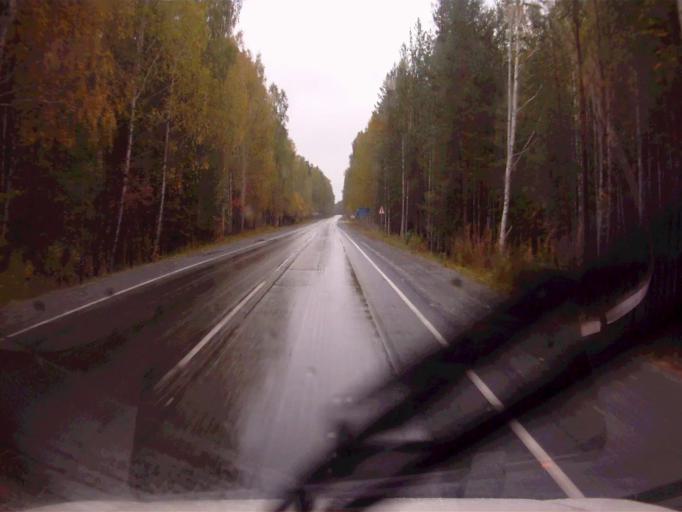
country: RU
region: Chelyabinsk
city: Tayginka
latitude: 55.5841
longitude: 60.6365
